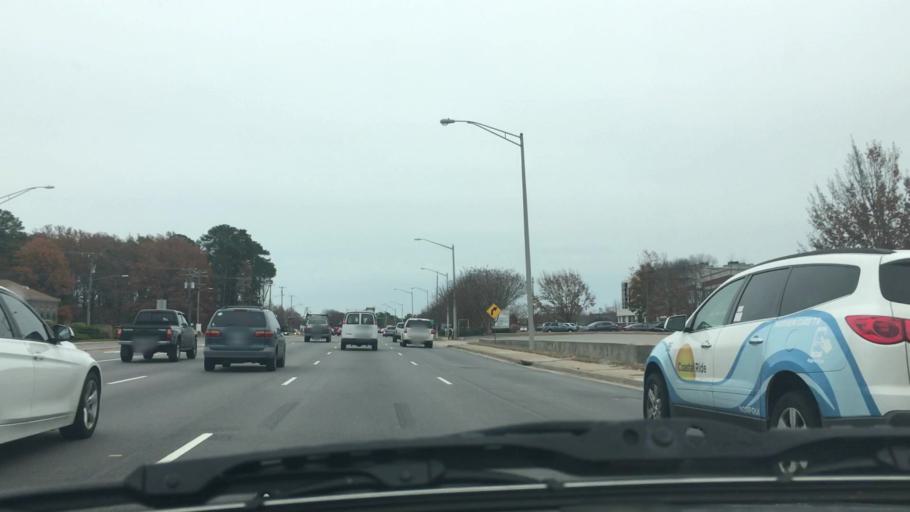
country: US
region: Virginia
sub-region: City of Chesapeake
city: Chesapeake
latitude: 36.8253
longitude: -76.1297
